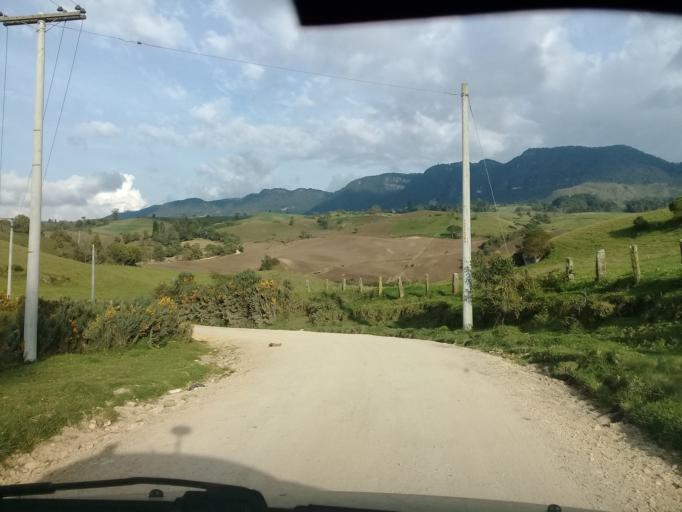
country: CO
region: Cundinamarca
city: Sibate
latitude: 4.4288
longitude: -74.2880
